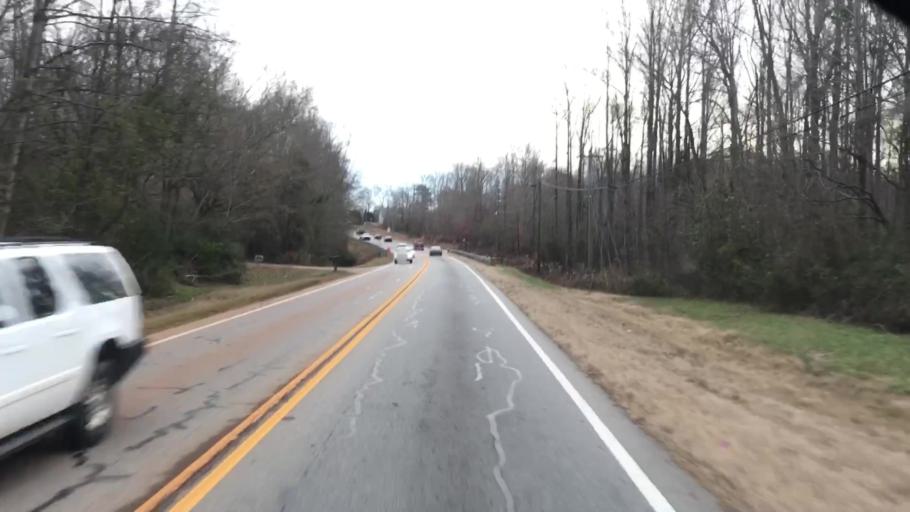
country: US
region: Georgia
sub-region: Jackson County
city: Hoschton
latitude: 34.0521
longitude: -83.7793
